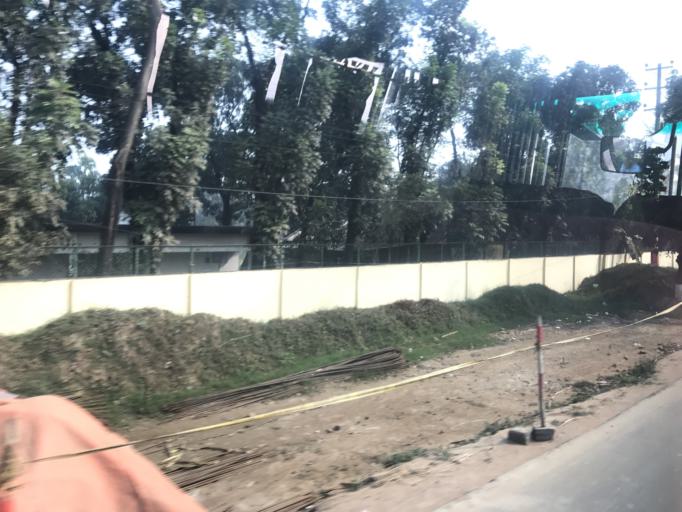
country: BD
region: Dhaka
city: Tungi
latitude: 23.9016
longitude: 90.2690
